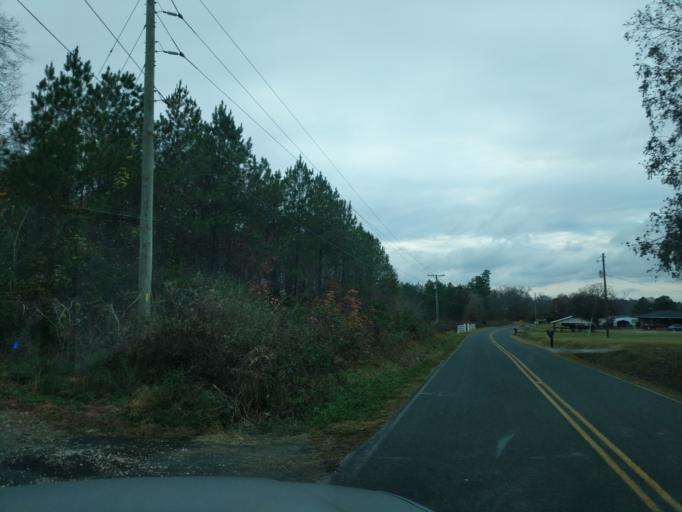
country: US
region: South Carolina
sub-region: Laurens County
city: Clinton
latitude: 34.4031
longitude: -81.9385
